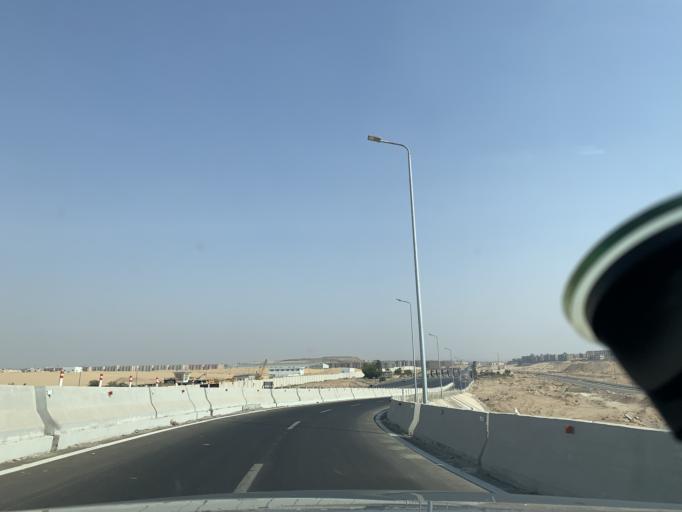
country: EG
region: Muhafazat al Qalyubiyah
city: Al Khankah
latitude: 30.2012
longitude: 31.4196
